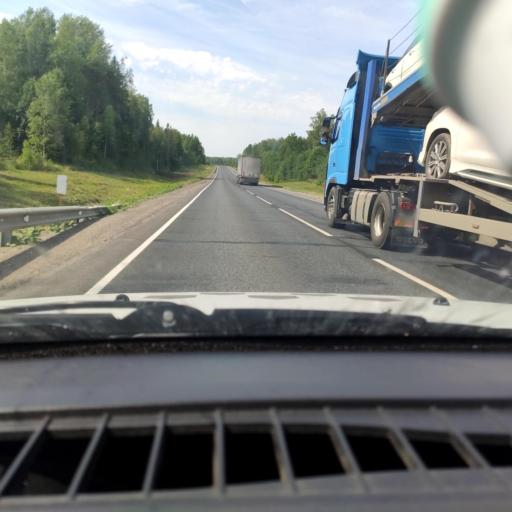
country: RU
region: Kirov
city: Kostino
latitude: 58.7190
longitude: 53.6707
